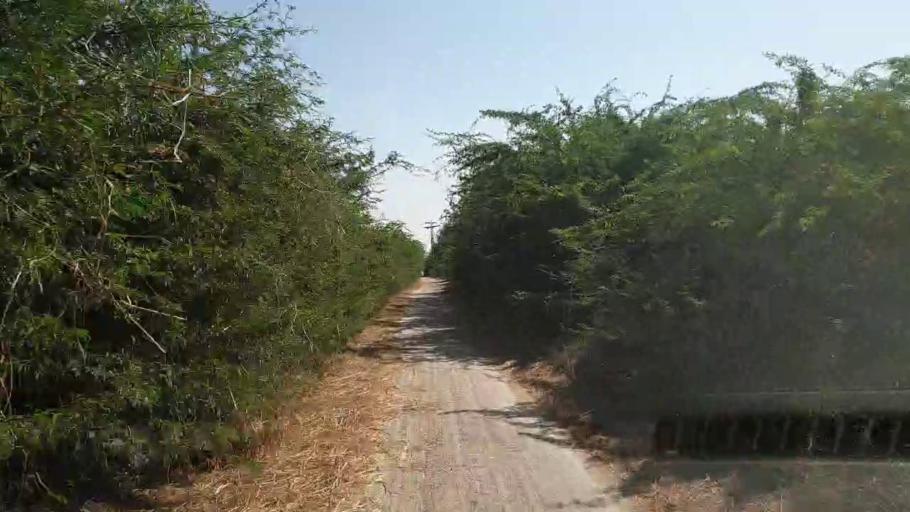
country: PK
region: Sindh
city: Tando Bago
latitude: 24.6465
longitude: 68.9860
